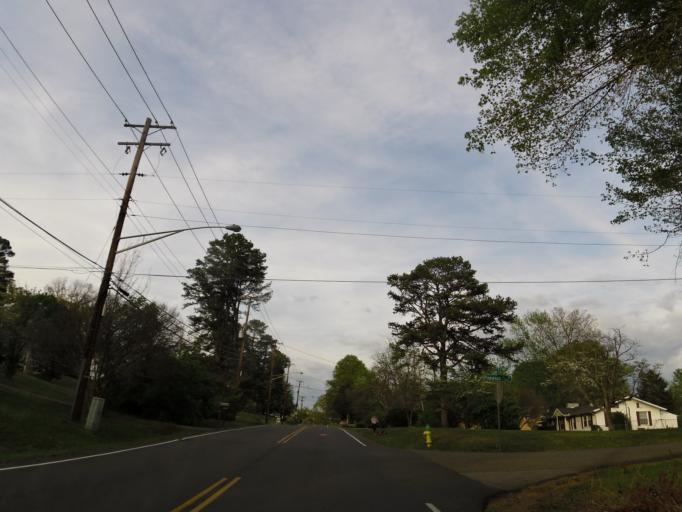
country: US
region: Tennessee
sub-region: Knox County
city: Knoxville
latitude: 36.0497
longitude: -83.9132
